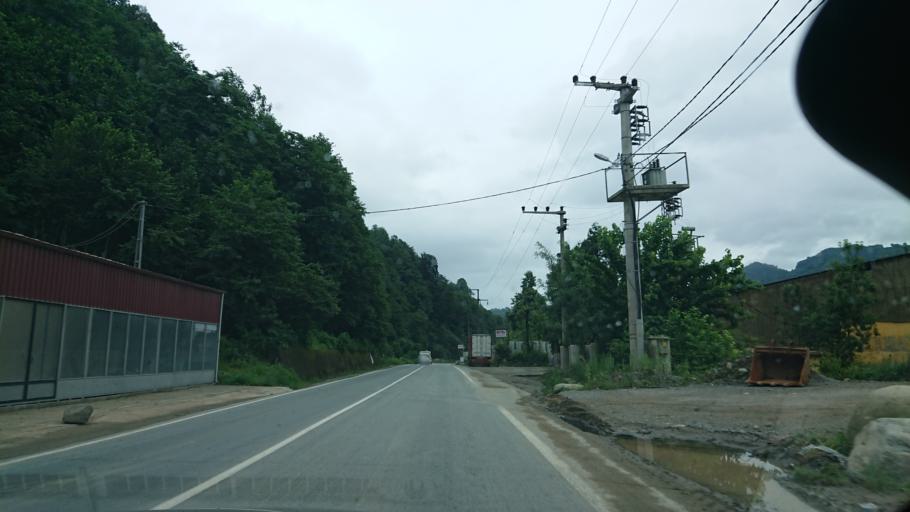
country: TR
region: Rize
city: Gundogdu
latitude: 41.0150
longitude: 40.5674
